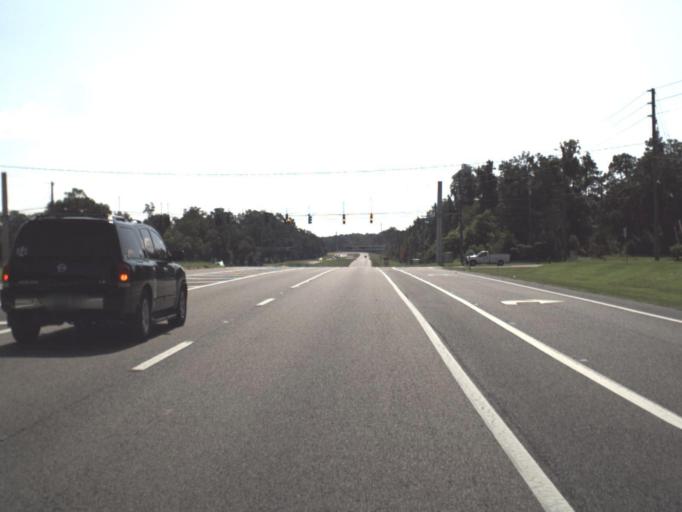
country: US
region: Florida
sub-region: Hernando County
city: South Brooksville
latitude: 28.5382
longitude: -82.3890
